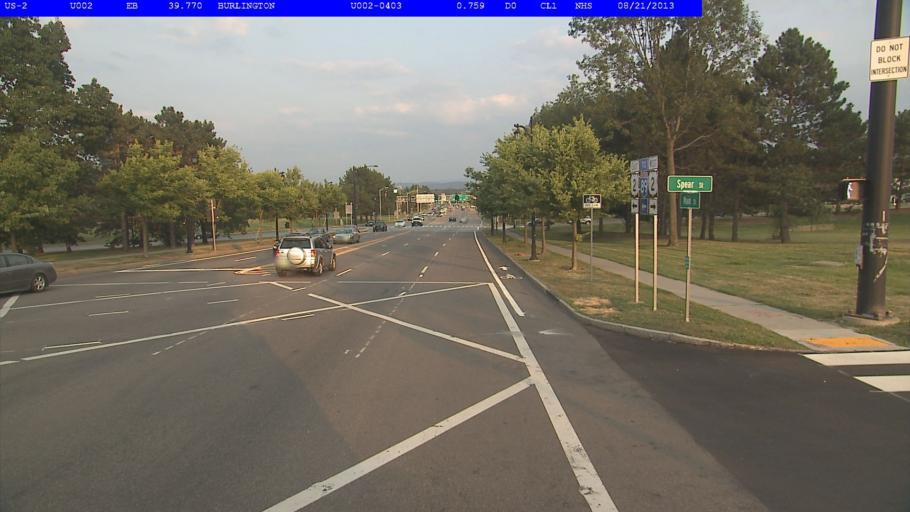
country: US
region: Vermont
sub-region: Chittenden County
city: Winooski
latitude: 44.4730
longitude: -73.1914
